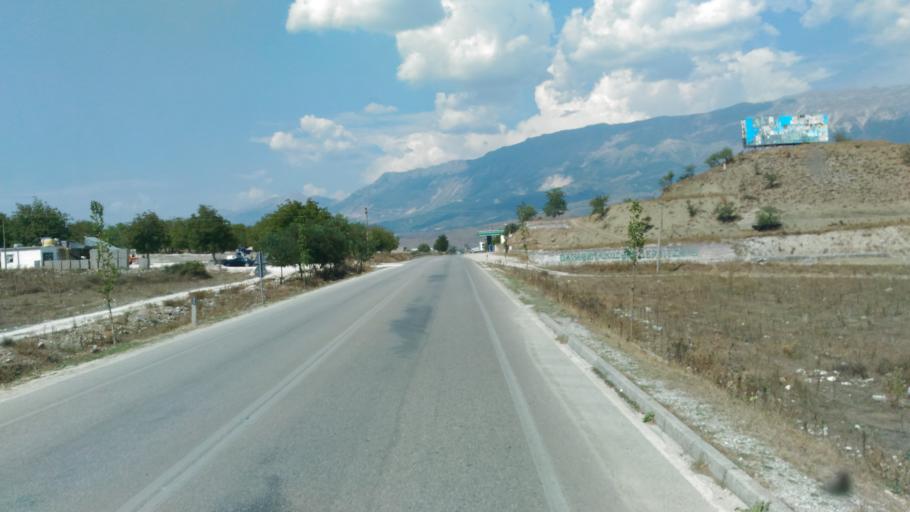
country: AL
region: Gjirokaster
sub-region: Rrethi i Gjirokastres
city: Dervician
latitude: 40.0434
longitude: 20.1760
